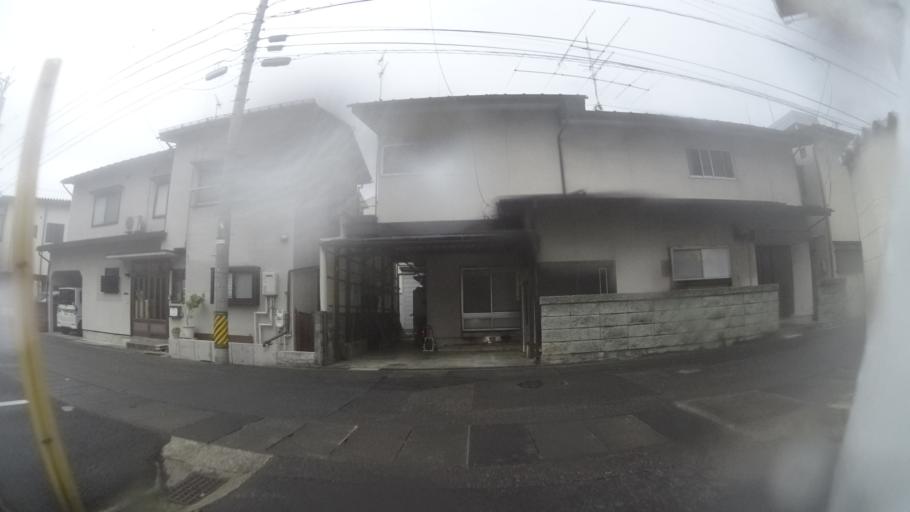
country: JP
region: Nagano
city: Nagano-shi
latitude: 36.6525
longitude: 138.2002
